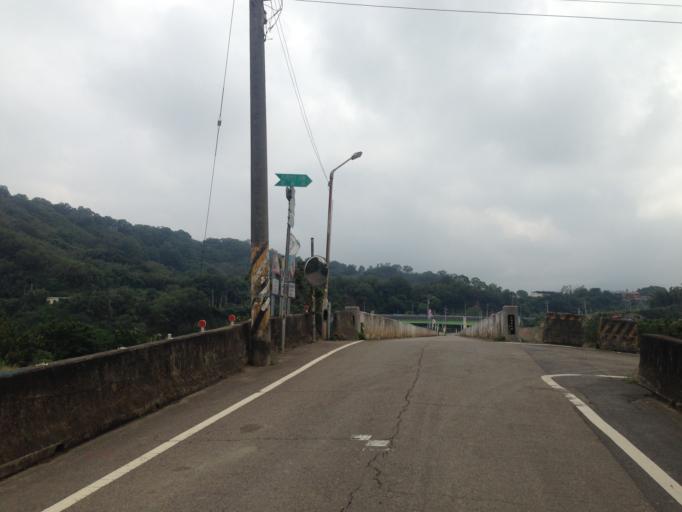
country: TW
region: Taiwan
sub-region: Hsinchu
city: Hsinchu
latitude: 24.6736
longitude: 120.9626
